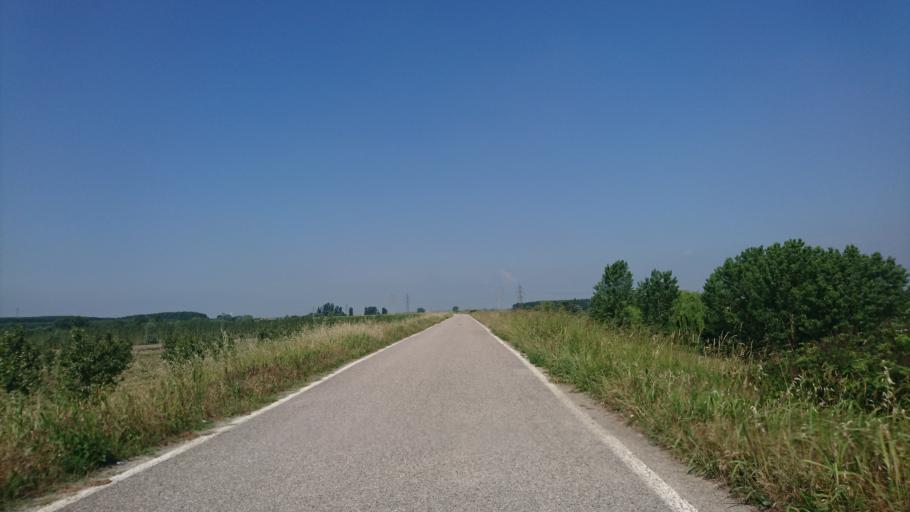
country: IT
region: Lombardy
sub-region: Provincia di Mantova
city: Ostiglia
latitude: 45.0756
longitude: 11.1181
